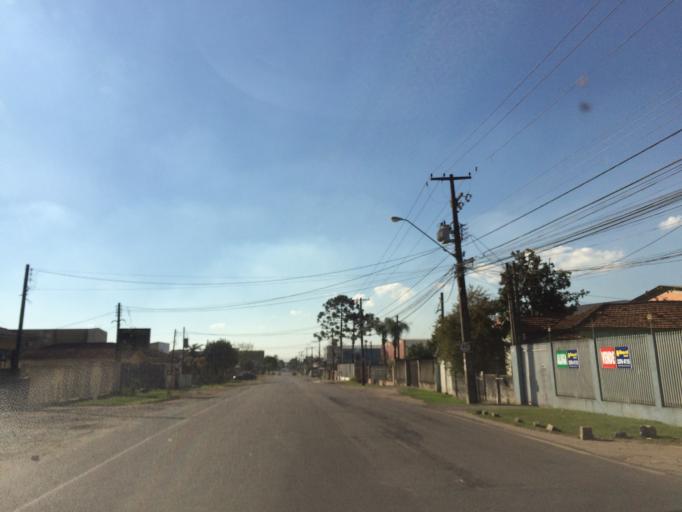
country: BR
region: Parana
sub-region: Sao Jose Dos Pinhais
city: Sao Jose dos Pinhais
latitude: -25.5045
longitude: -49.2348
